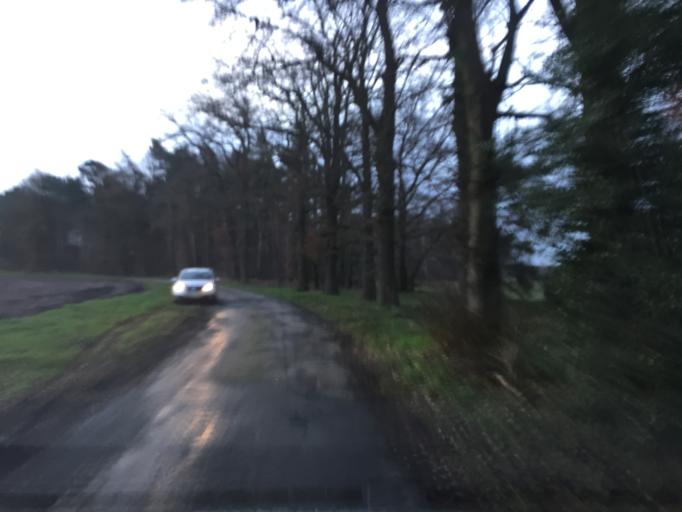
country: DE
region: Lower Saxony
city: Kirchdorf
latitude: 52.6123
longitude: 8.8654
